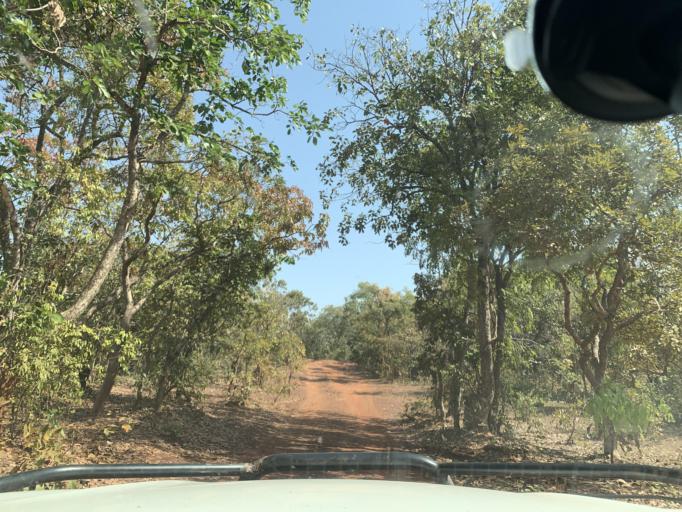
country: ML
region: Sikasso
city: Kolondieba
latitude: 10.8951
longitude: -6.7453
